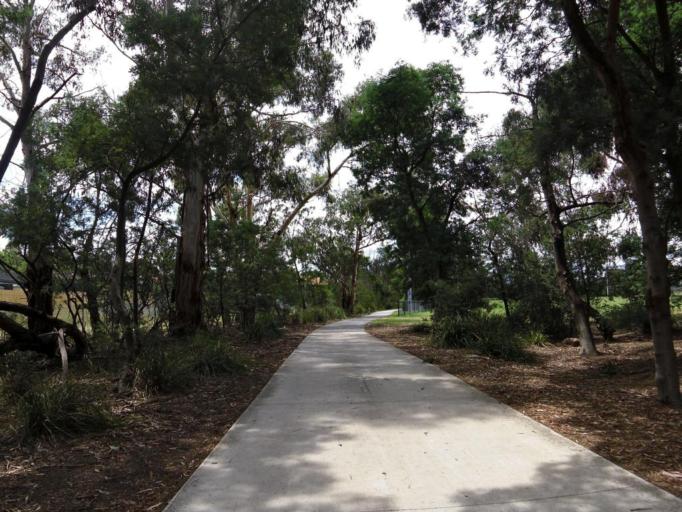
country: AU
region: Victoria
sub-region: Monash
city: Ashwood
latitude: -37.8717
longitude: 145.0947
